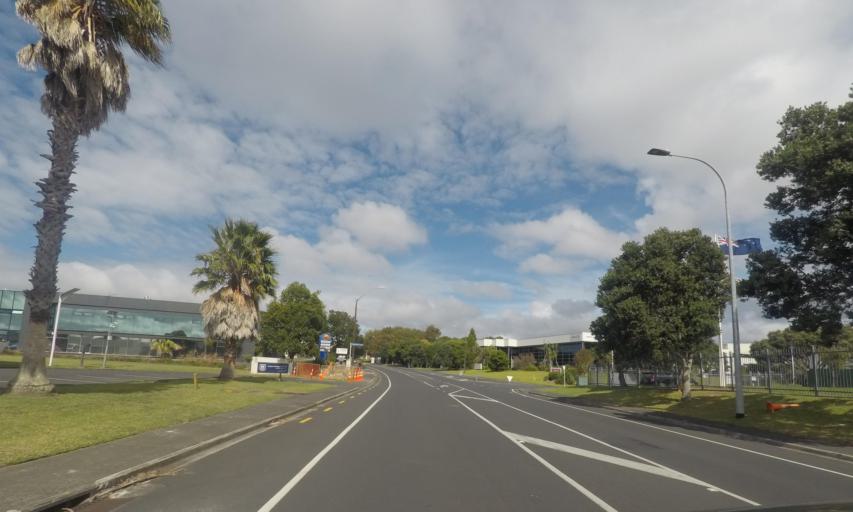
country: NZ
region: Auckland
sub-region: Auckland
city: Rothesay Bay
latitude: -36.7494
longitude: 174.7008
